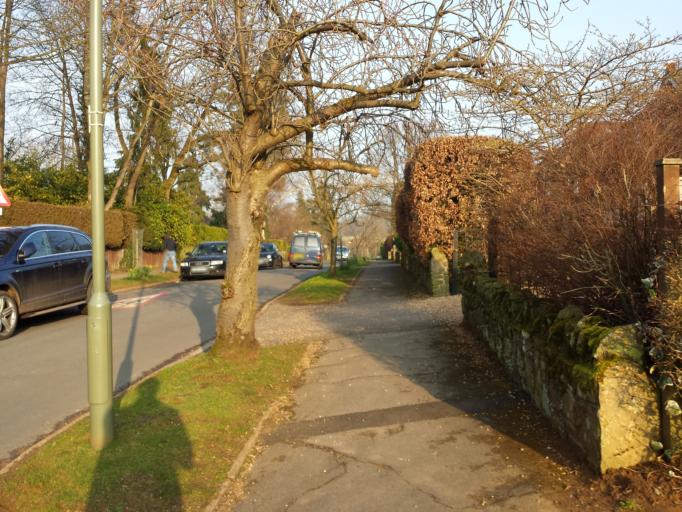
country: GB
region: England
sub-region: Surrey
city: Godalming
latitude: 51.1774
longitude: -0.6051
